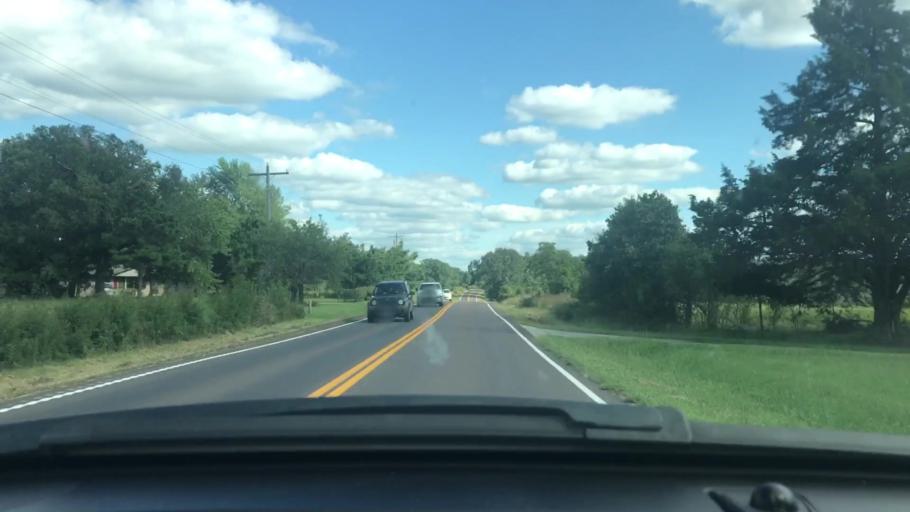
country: US
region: Missouri
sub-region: Wright County
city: Mountain Grove
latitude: 37.2331
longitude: -92.2987
